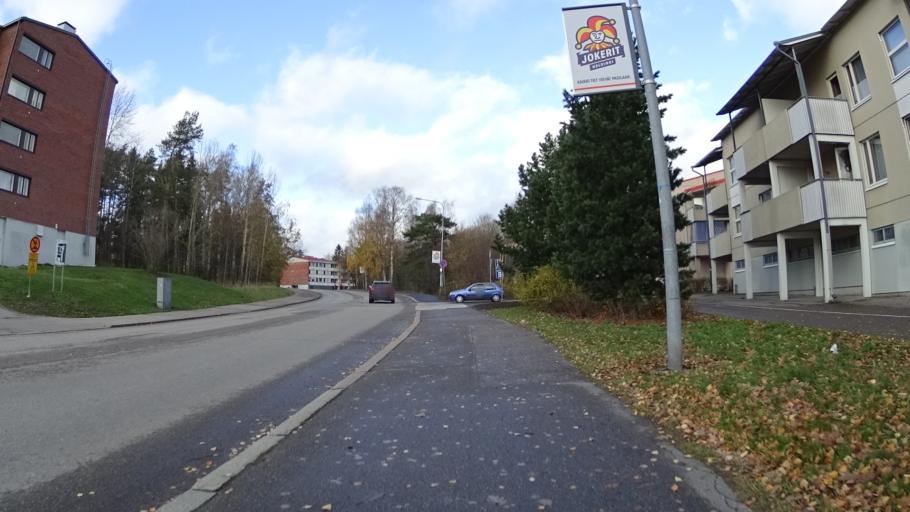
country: FI
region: Uusimaa
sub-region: Helsinki
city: Teekkarikylae
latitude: 60.2388
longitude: 24.8882
